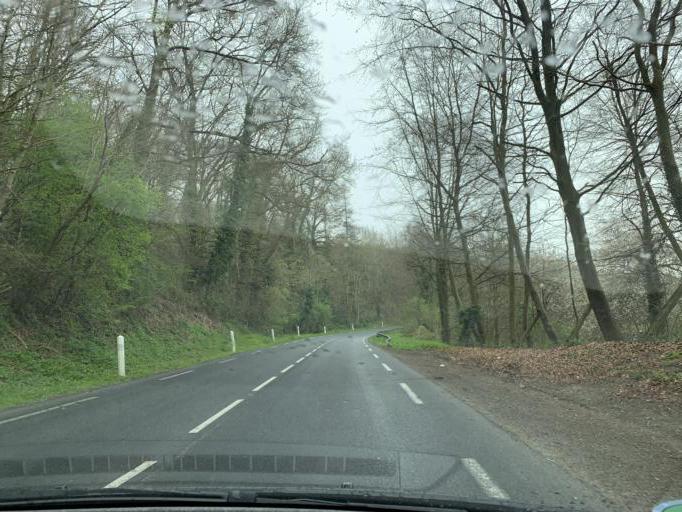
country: FR
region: Haute-Normandie
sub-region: Departement de la Seine-Maritime
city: Cany-Barville
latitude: 49.7869
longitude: 0.6474
